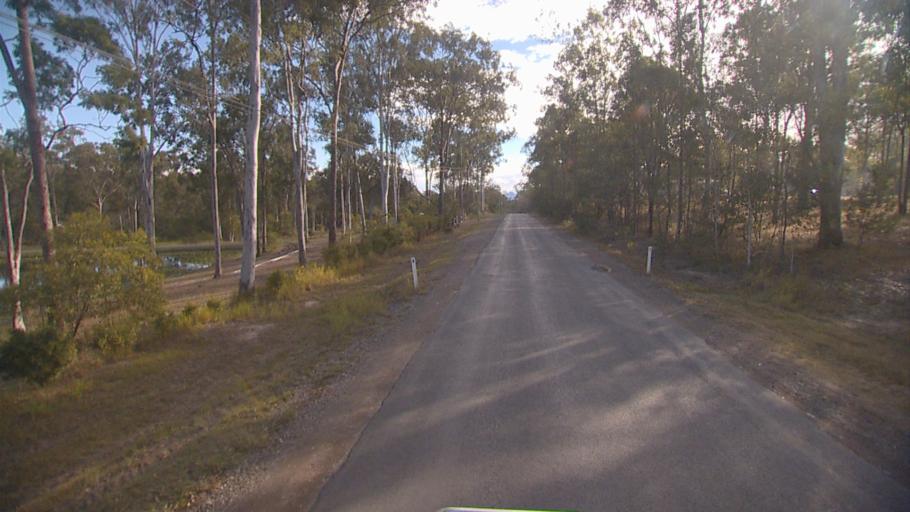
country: AU
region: Queensland
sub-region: Logan
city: Cedar Vale
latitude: -27.8338
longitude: 153.0589
